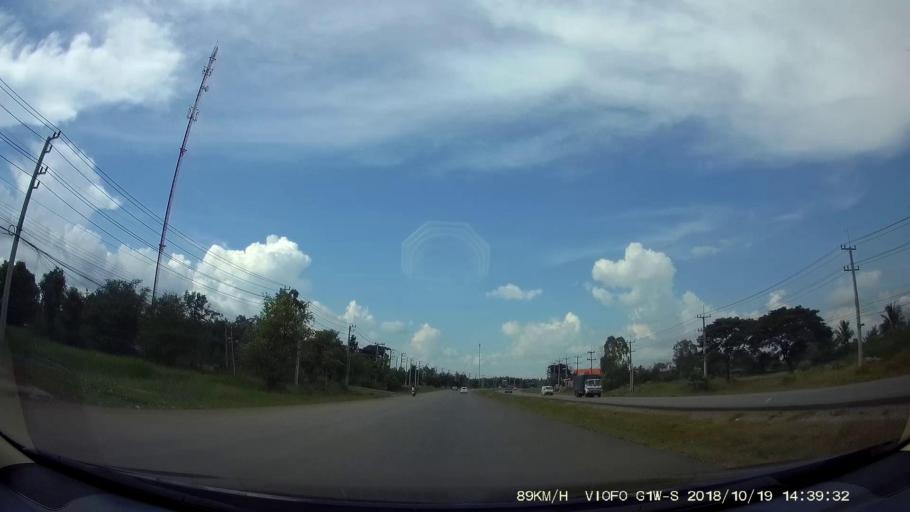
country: TH
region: Chaiyaphum
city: Kaeng Khro
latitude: 16.2273
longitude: 102.1948
